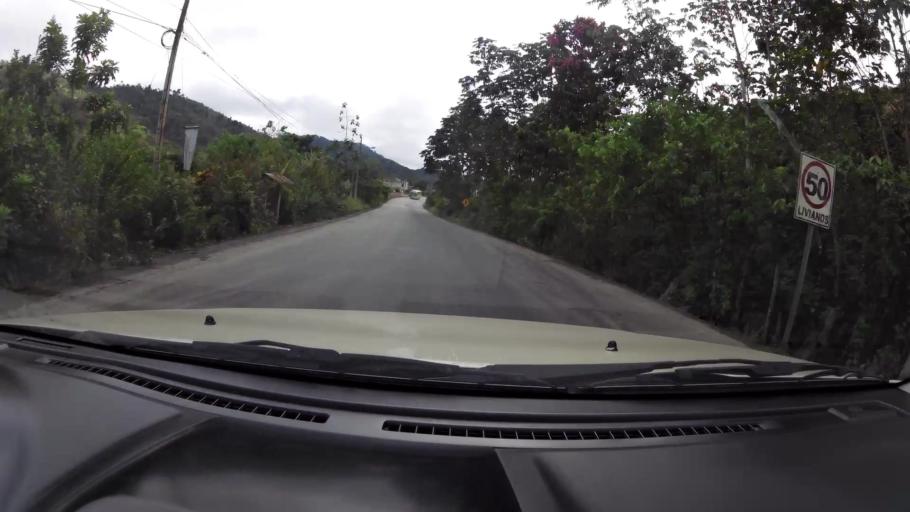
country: EC
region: El Oro
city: Pasaje
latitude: -3.3209
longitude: -79.6804
